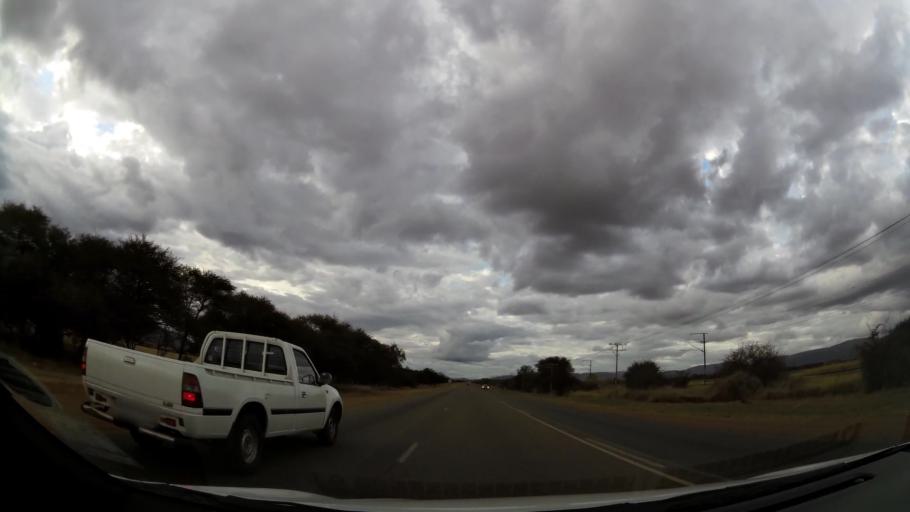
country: ZA
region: Limpopo
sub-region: Waterberg District Municipality
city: Mokopane
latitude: -24.2672
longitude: 28.9828
